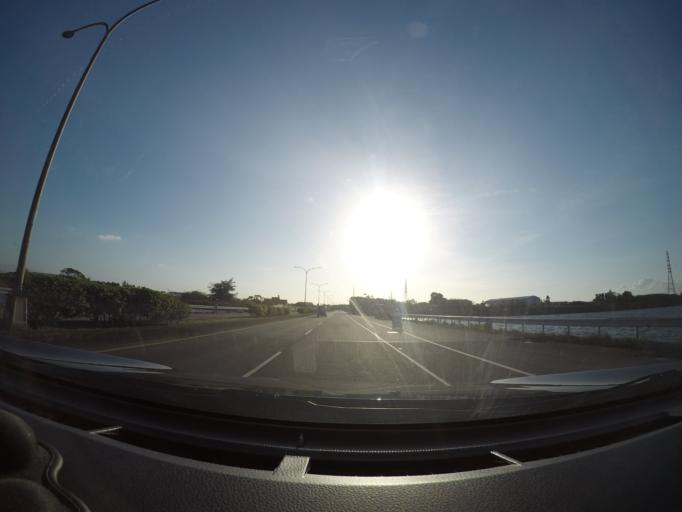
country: TW
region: Taiwan
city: Taoyuan City
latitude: 25.0750
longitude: 121.2025
